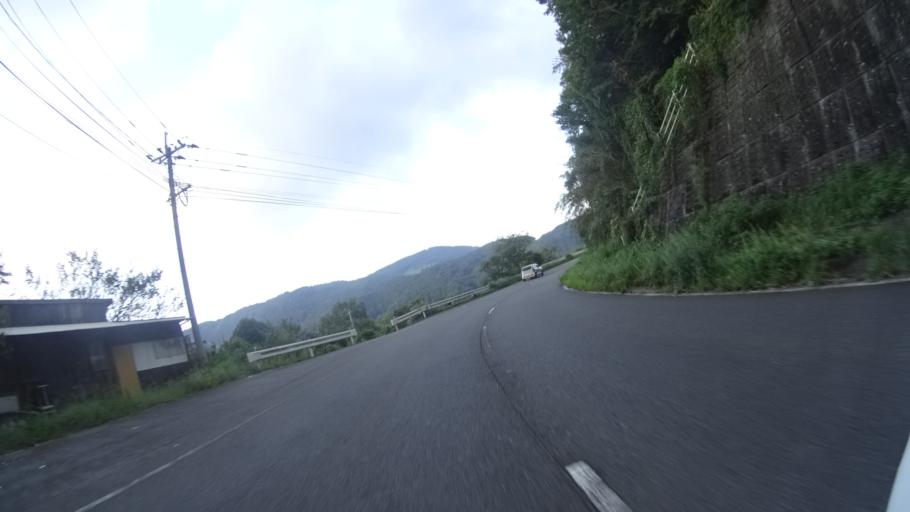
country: JP
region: Oita
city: Beppu
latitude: 33.3376
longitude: 131.4013
